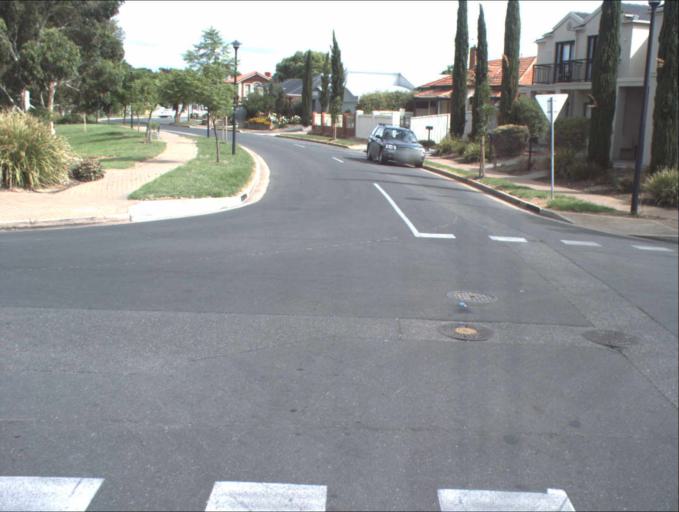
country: AU
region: South Australia
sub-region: Port Adelaide Enfield
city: Blair Athol
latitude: -34.8690
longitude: 138.5901
